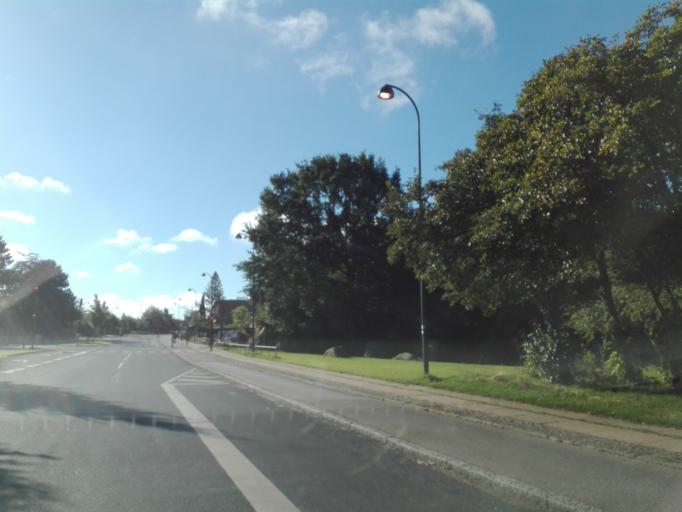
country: DK
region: Capital Region
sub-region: Lyngby-Tarbaek Kommune
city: Kongens Lyngby
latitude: 55.7467
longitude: 12.5224
